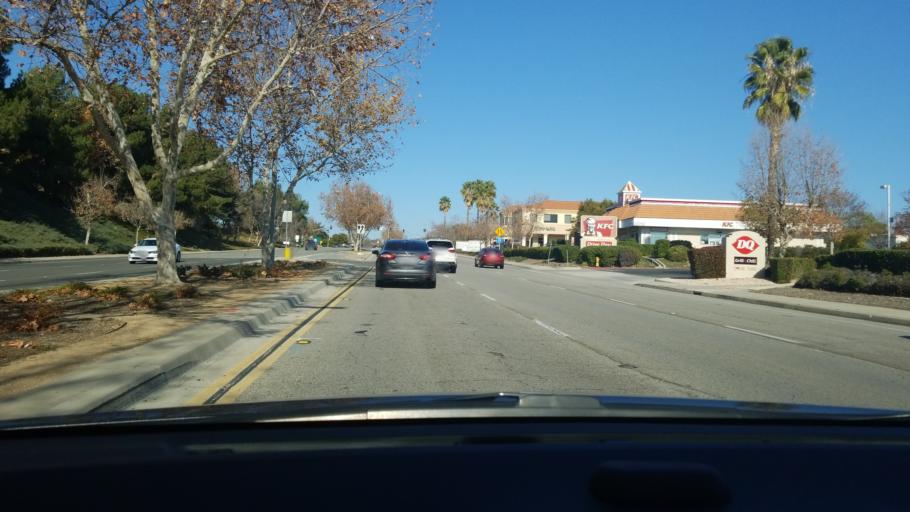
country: US
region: California
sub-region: Riverside County
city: Murrieta
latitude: 33.5698
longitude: -117.2050
